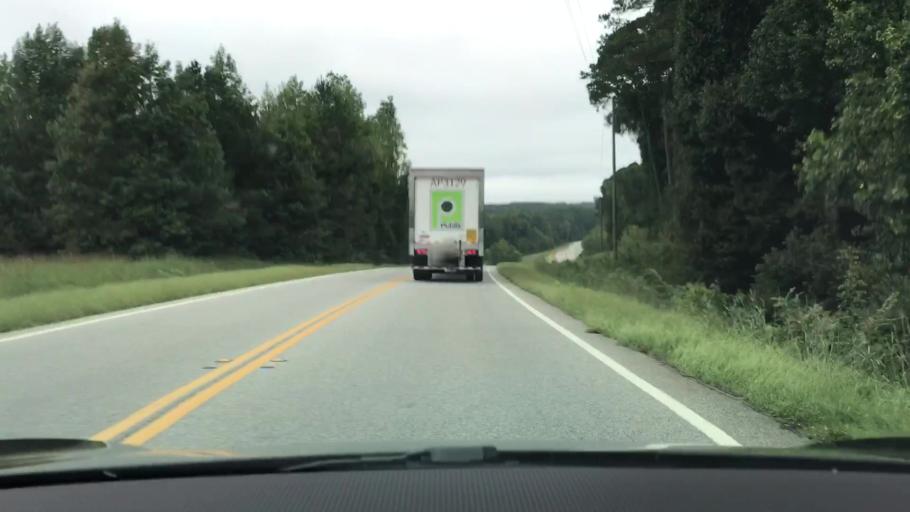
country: US
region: Georgia
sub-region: Greene County
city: Greensboro
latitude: 33.6677
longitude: -83.2571
